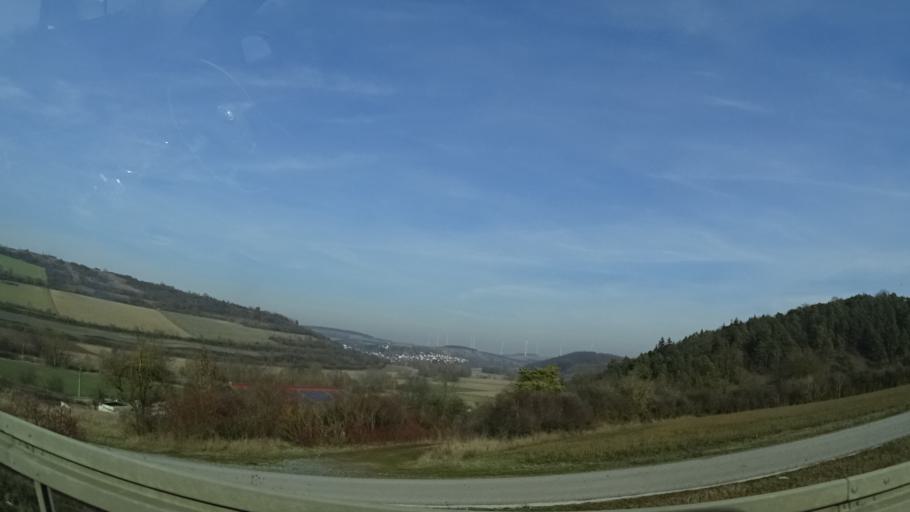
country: DE
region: Bavaria
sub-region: Regierungsbezirk Unterfranken
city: Heustreu
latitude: 50.3361
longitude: 10.2481
